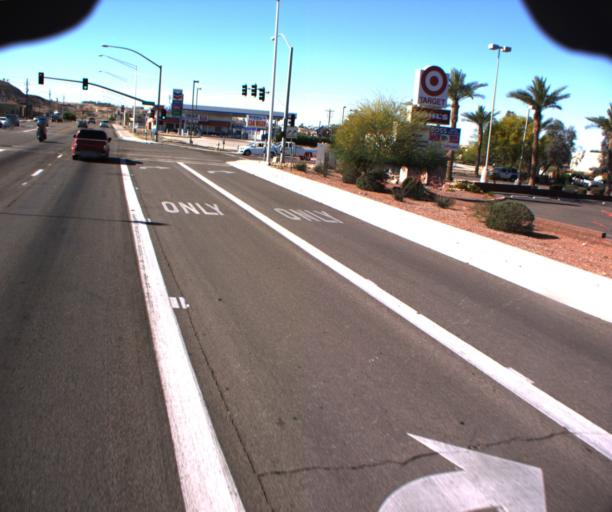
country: US
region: Arizona
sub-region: Mohave County
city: Bullhead City
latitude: 35.0526
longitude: -114.5892
